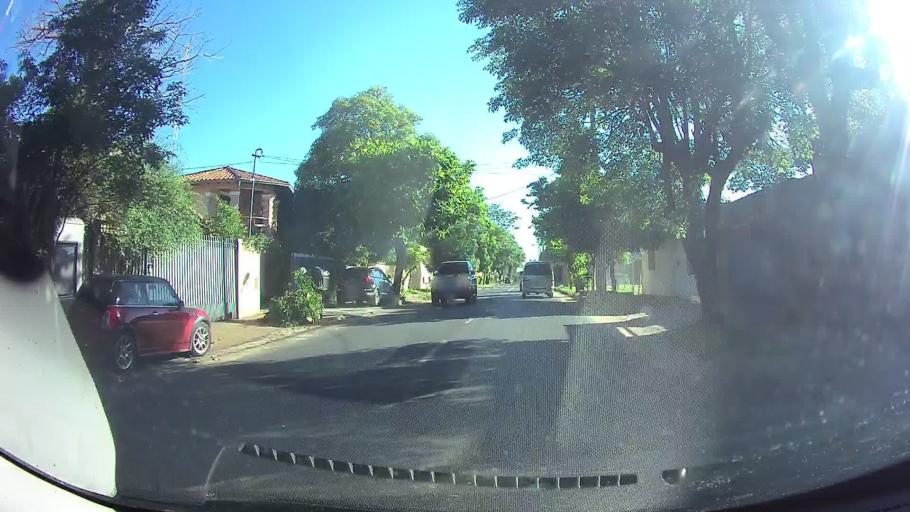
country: PY
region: Central
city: Fernando de la Mora
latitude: -25.2948
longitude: -57.5581
